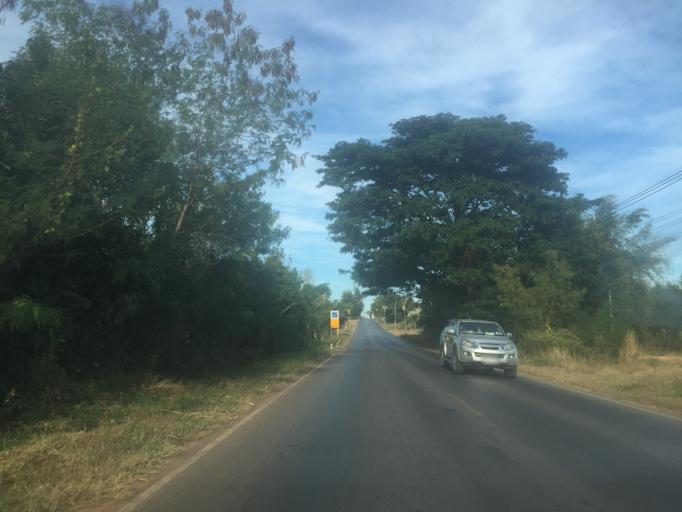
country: TH
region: Changwat Udon Thani
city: Si That
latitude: 16.9798
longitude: 103.1881
